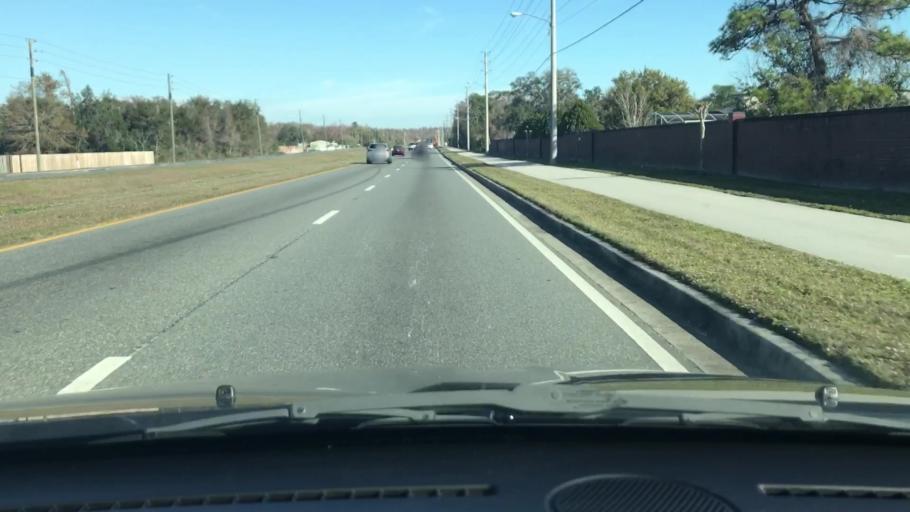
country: US
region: Florida
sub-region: Osceola County
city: Campbell
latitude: 28.2156
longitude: -81.4401
